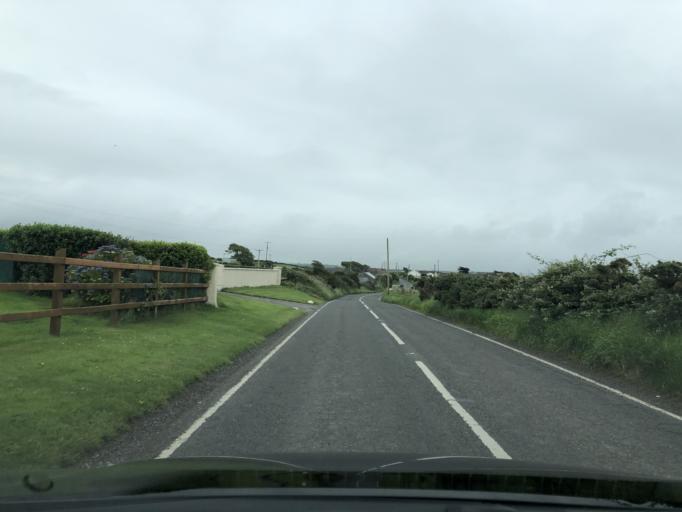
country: GB
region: Northern Ireland
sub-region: Down District
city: Dundrum
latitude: 54.2537
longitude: -5.7607
